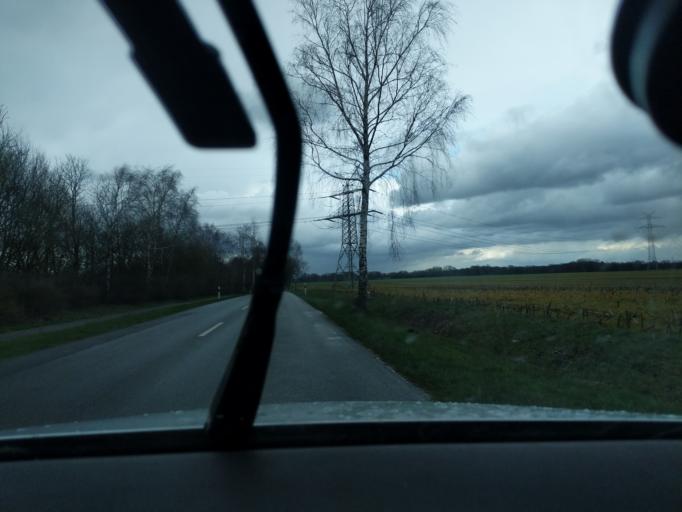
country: DE
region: Lower Saxony
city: Kutenholz
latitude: 53.5086
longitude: 9.3623
